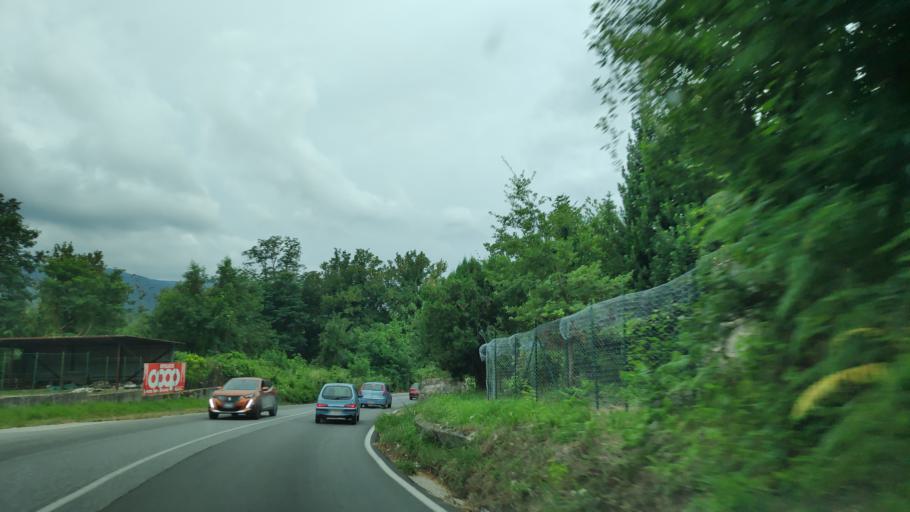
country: IT
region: Calabria
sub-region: Provincia di Vibo-Valentia
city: Brognaturo
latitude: 38.5871
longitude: 16.3365
